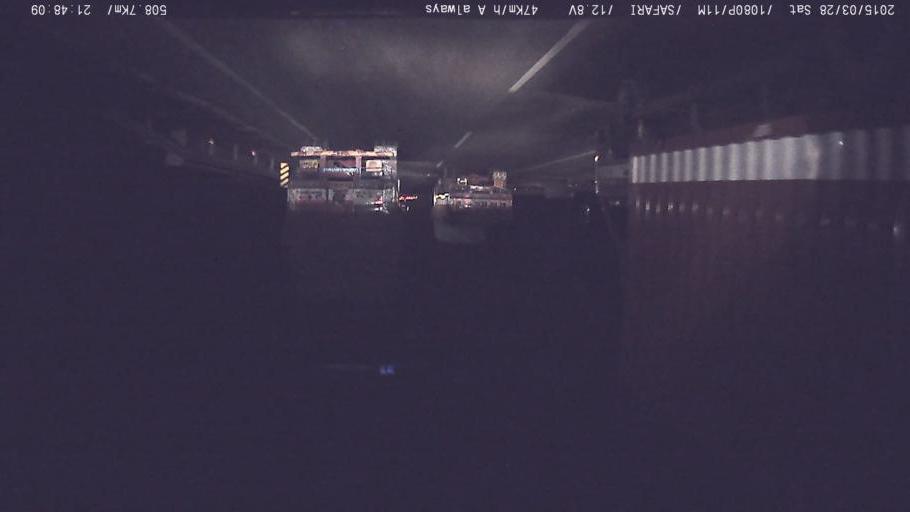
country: IN
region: Karnataka
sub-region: Bangalore Urban
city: Bangalore
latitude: 12.8692
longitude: 77.5038
